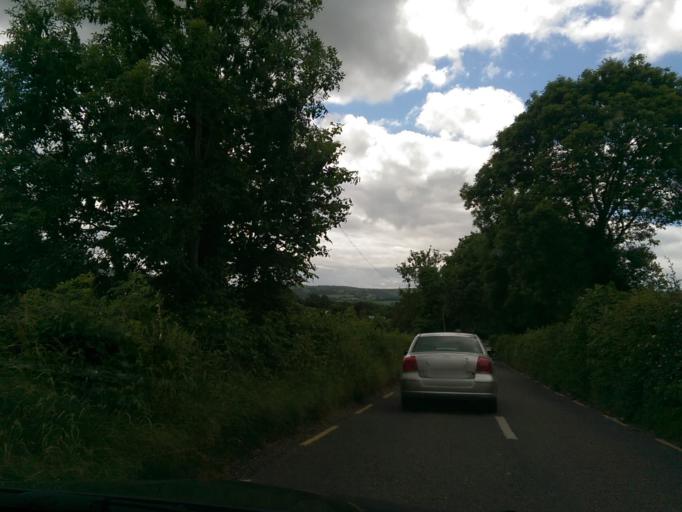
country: IE
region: Munster
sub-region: North Tipperary
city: Nenagh
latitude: 52.8159
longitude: -8.1940
